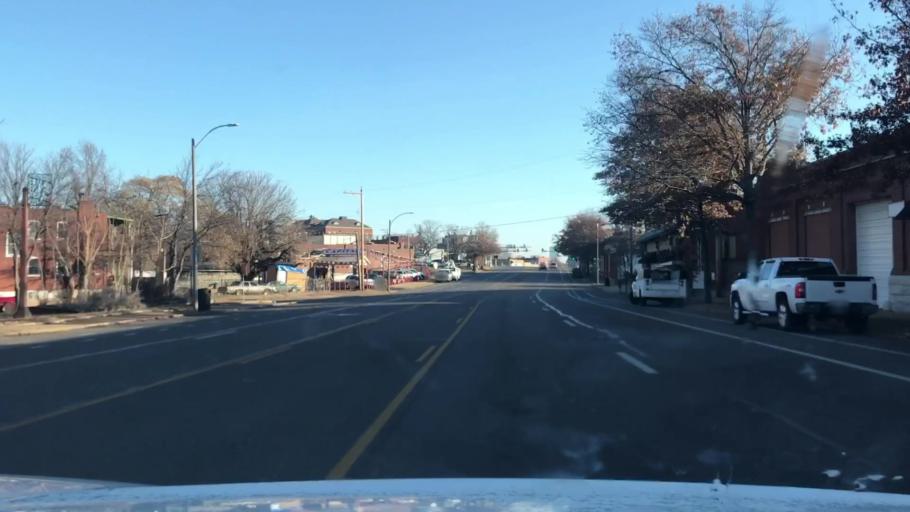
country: US
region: Missouri
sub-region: City of Saint Louis
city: St. Louis
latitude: 38.5994
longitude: -90.2346
